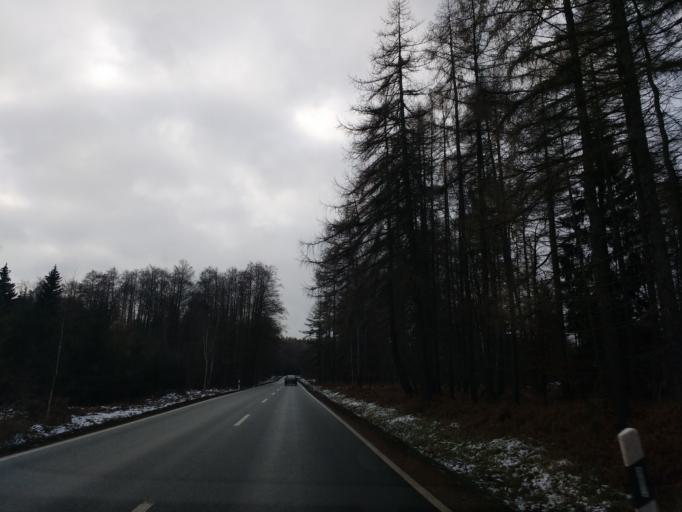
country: DE
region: Saxony-Anhalt
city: Friedrichsbrunn
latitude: 51.7046
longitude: 11.0681
